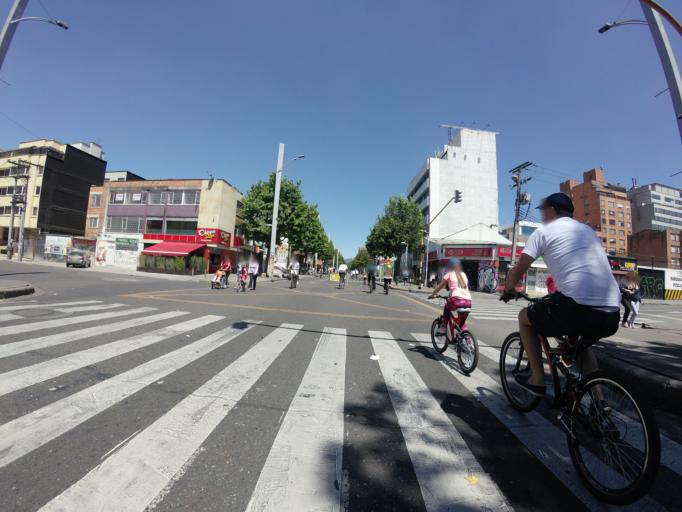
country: CO
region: Bogota D.C.
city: Barrio San Luis
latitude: 4.6602
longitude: -74.0609
